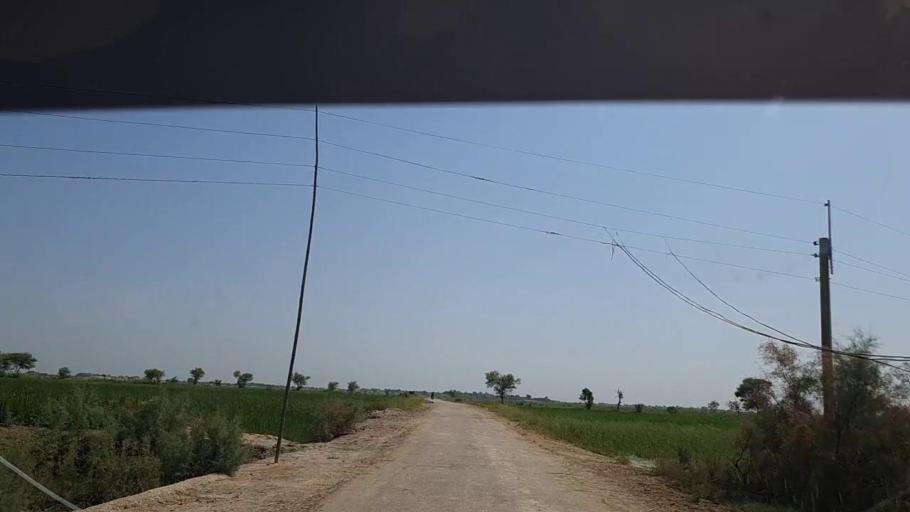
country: PK
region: Sindh
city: Kandhkot
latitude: 28.1815
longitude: 69.1590
